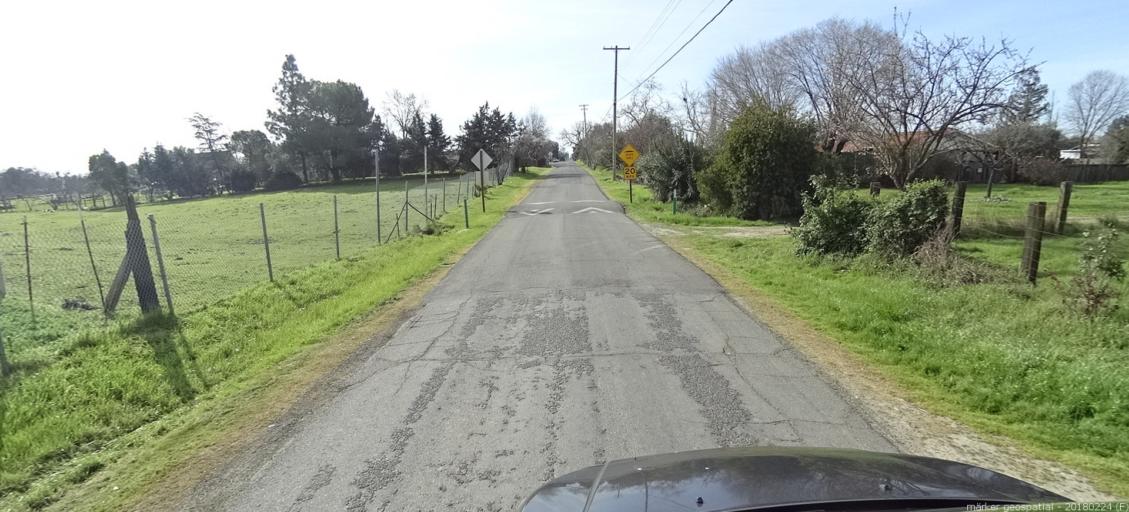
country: US
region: California
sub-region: Sacramento County
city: Rio Linda
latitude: 38.6954
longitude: -121.4615
